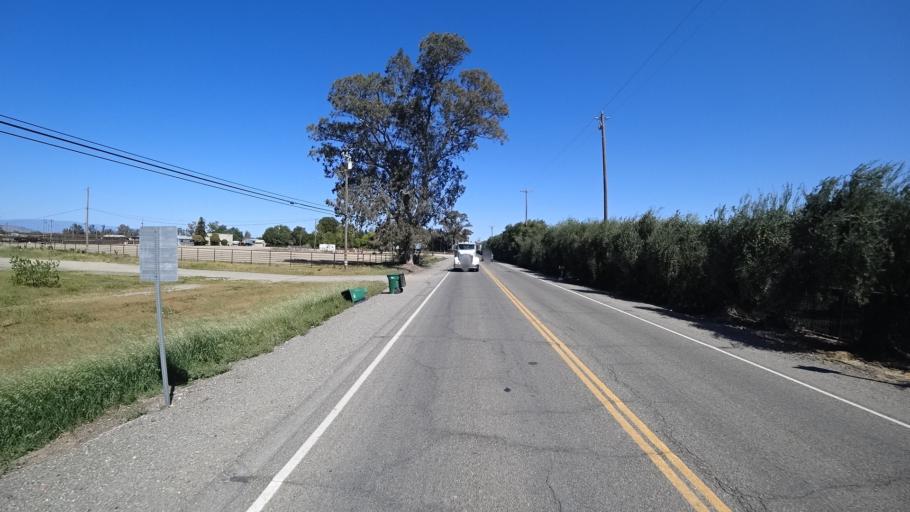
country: US
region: California
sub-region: Glenn County
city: Orland
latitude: 39.6995
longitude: -122.1966
